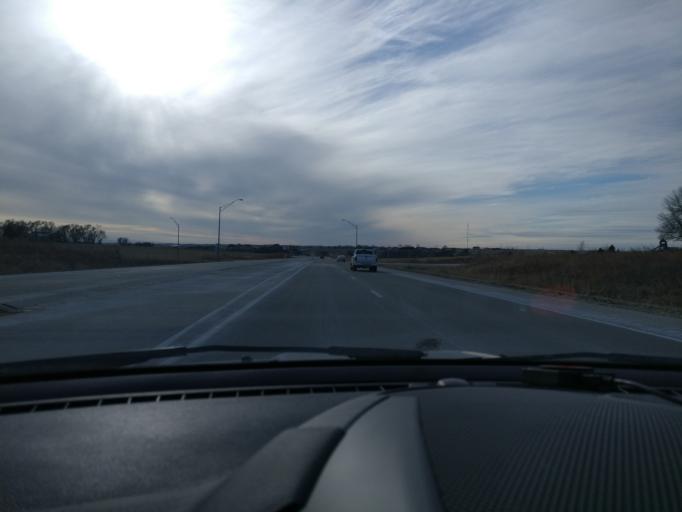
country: US
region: Nebraska
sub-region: Saunders County
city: Wahoo
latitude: 41.2327
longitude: -96.6299
